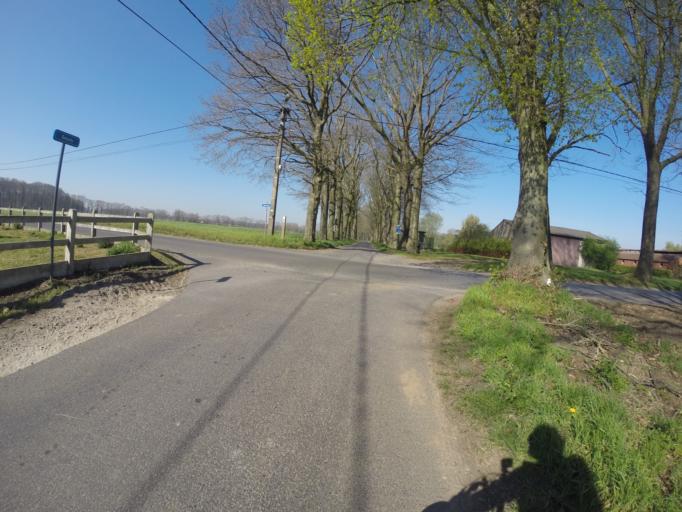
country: BE
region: Flanders
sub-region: Provincie West-Vlaanderen
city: Beernem
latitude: 51.1055
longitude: 3.3521
